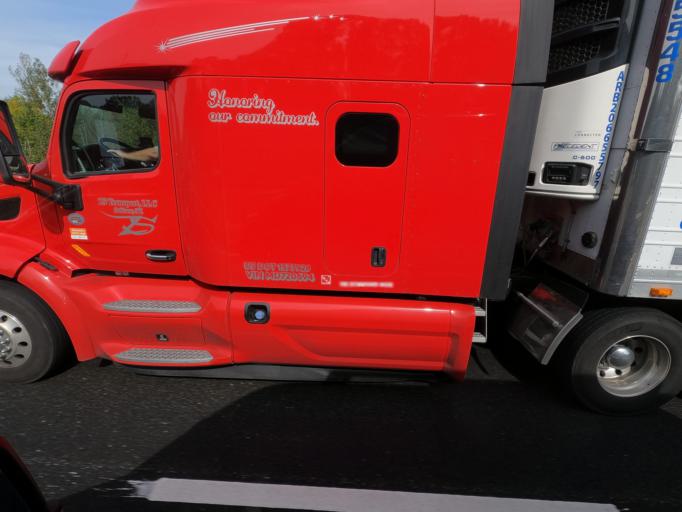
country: US
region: Tennessee
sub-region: Decatur County
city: Parsons
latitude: 35.8192
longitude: -88.1550
